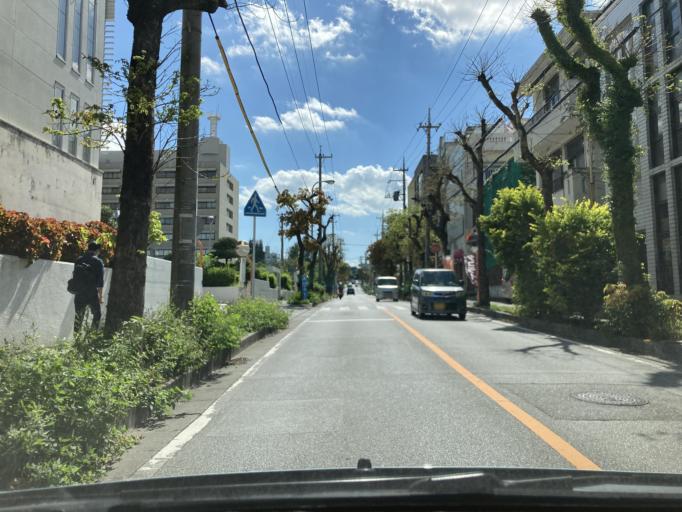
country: JP
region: Okinawa
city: Naha-shi
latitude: 26.2089
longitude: 127.6860
